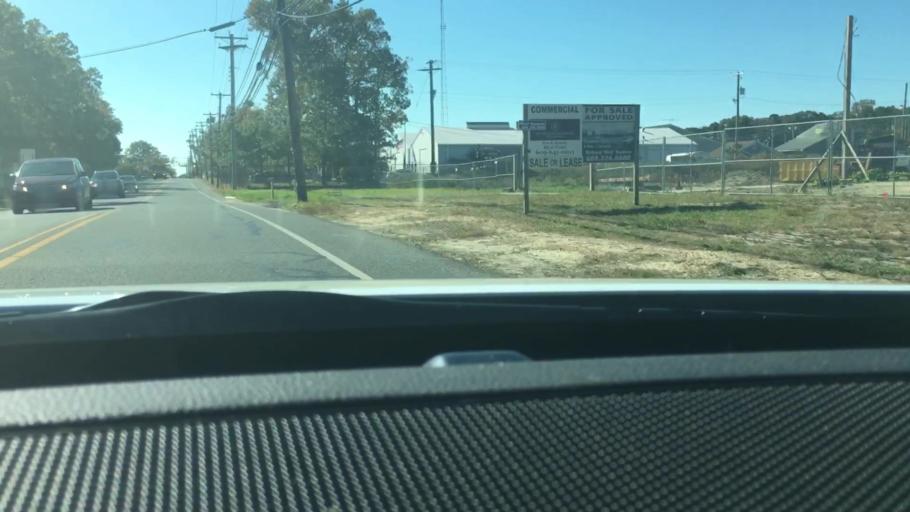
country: US
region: New Jersey
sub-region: Atlantic County
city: Northfield
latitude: 39.3829
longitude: -74.5434
